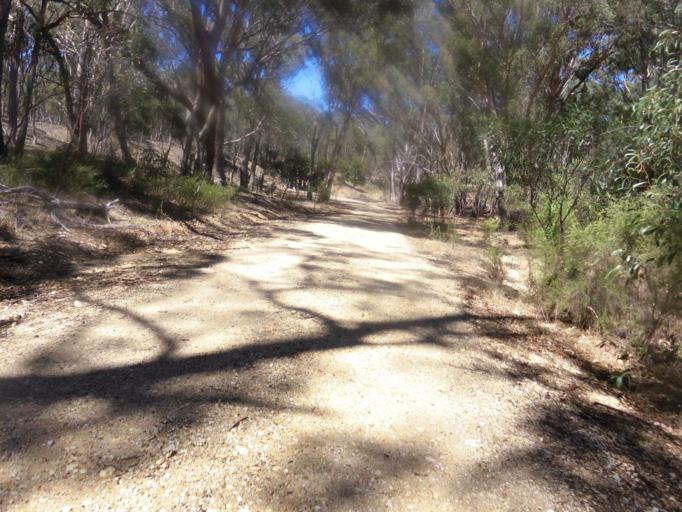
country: AU
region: Victoria
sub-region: Mount Alexander
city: Castlemaine
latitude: -37.0456
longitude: 144.1802
